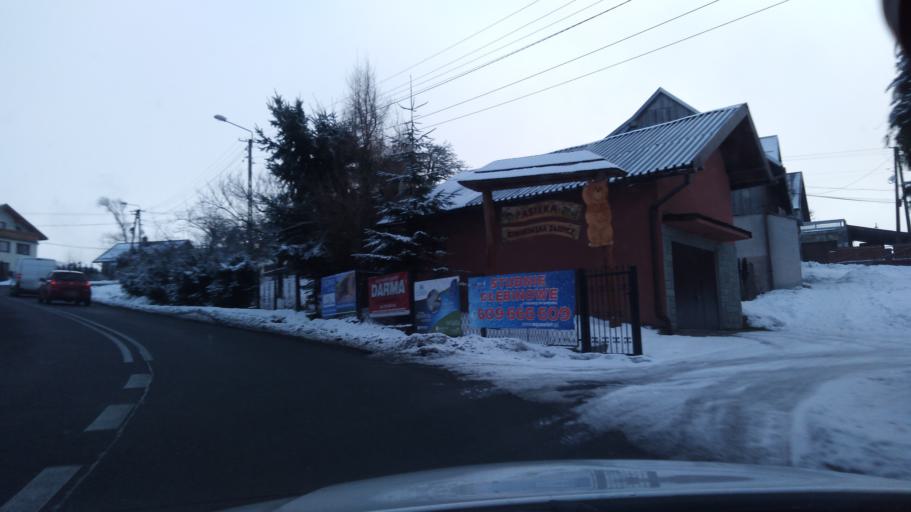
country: PL
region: Silesian Voivodeship
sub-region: Powiat cieszynski
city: Koniakow
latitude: 49.5495
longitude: 18.9258
